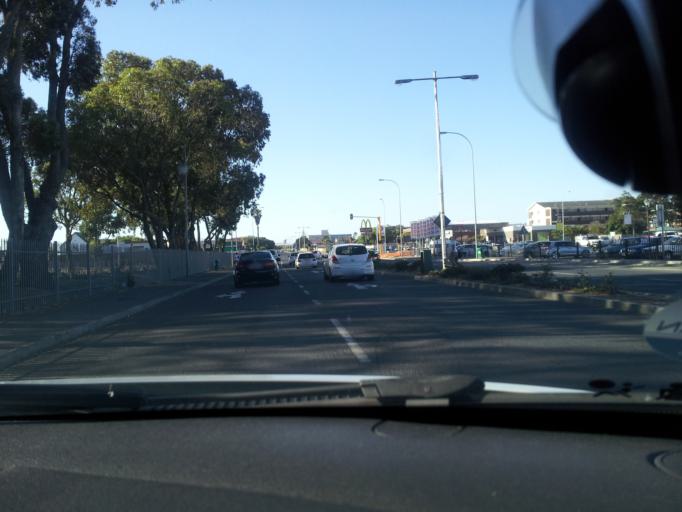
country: ZA
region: Western Cape
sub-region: Overberg District Municipality
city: Grabouw
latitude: -34.1227
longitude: 18.8361
